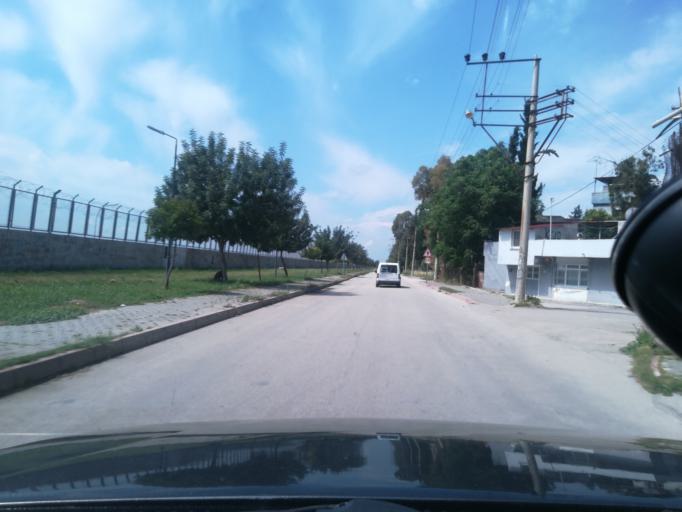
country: TR
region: Adana
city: Seyhan
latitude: 36.9840
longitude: 35.2803
